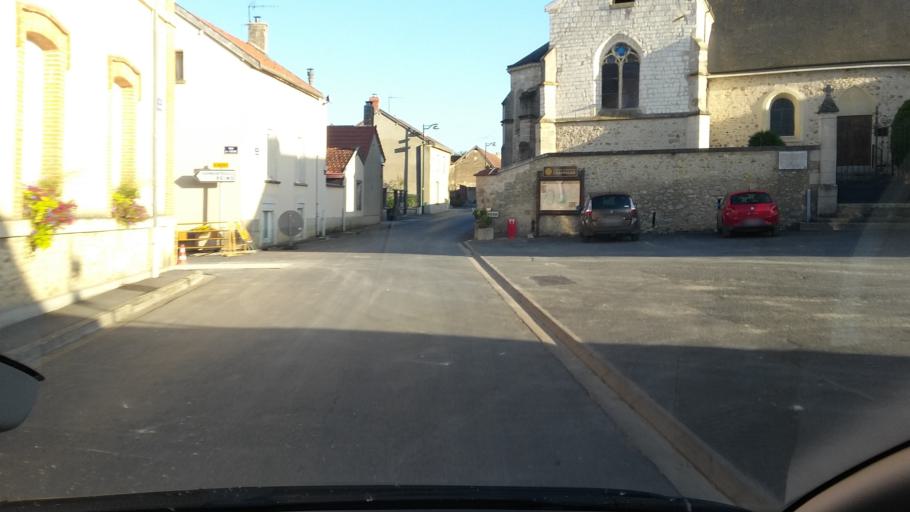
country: FR
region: Champagne-Ardenne
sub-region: Departement de la Marne
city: Cormontreuil
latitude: 49.1924
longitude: 4.0412
